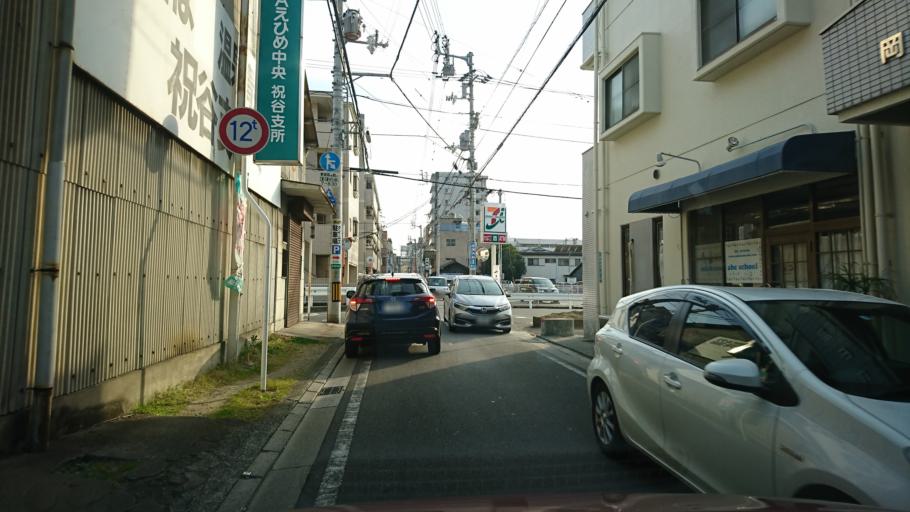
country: JP
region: Ehime
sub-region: Shikoku-chuo Shi
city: Matsuyama
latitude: 33.8521
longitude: 132.7761
